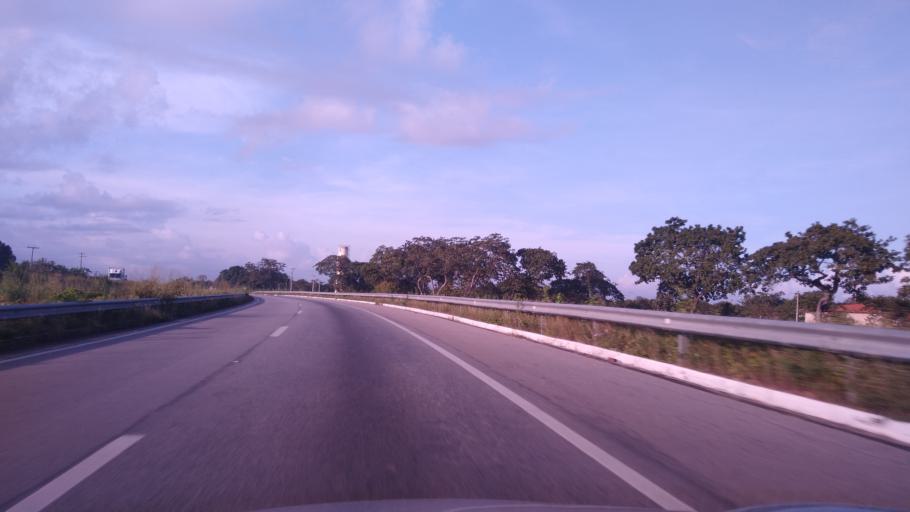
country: BR
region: Ceara
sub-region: Pacajus
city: Pacajus
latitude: -4.1699
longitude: -38.4932
